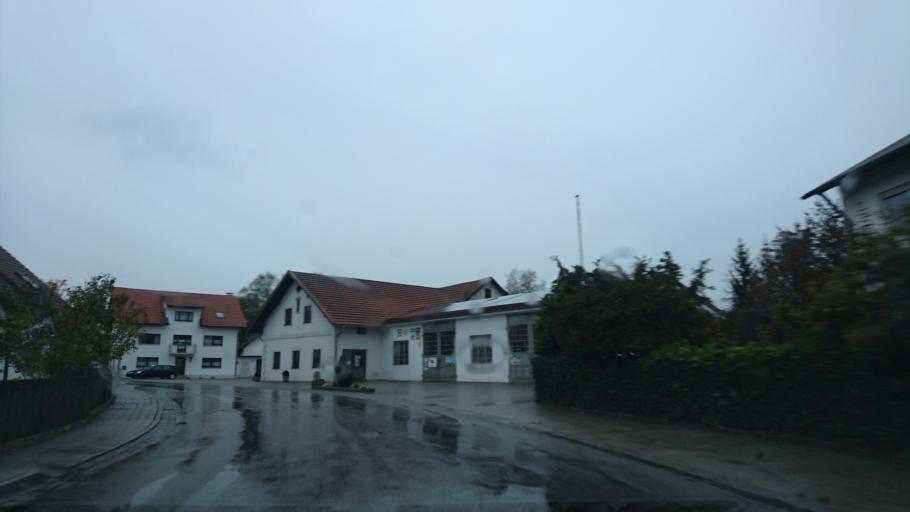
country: DE
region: Bavaria
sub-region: Upper Bavaria
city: Jetzendorf
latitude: 48.4345
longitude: 11.4234
